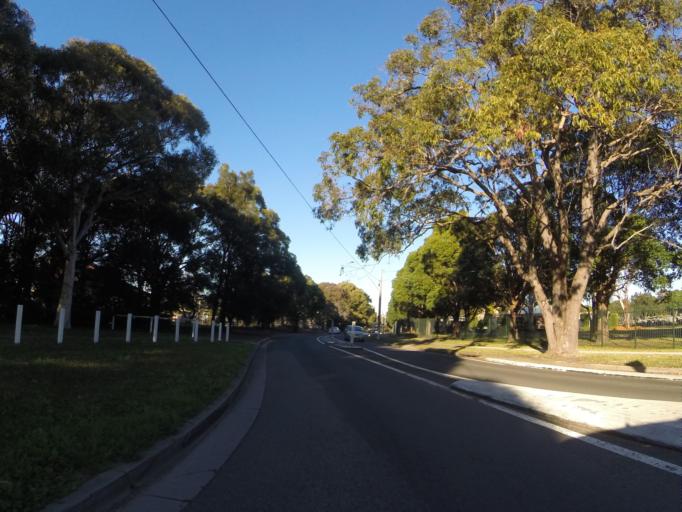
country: AU
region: New South Wales
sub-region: Sutherland Shire
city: Loftus
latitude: -34.0352
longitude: 151.0540
